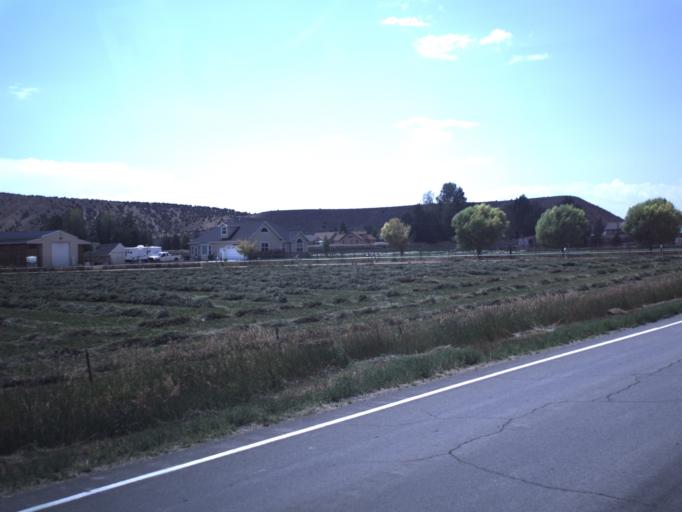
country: US
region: Utah
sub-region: Uintah County
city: Maeser
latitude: 40.4627
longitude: -109.6026
